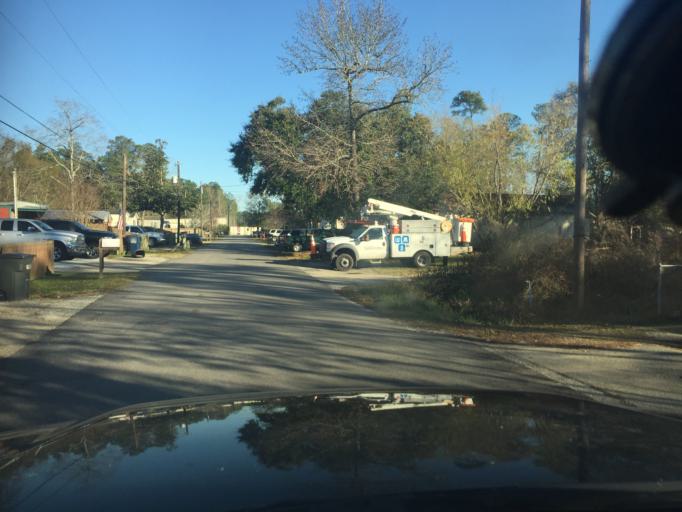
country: US
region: Louisiana
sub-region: Saint Tammany Parish
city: Slidell
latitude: 30.2535
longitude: -89.7645
